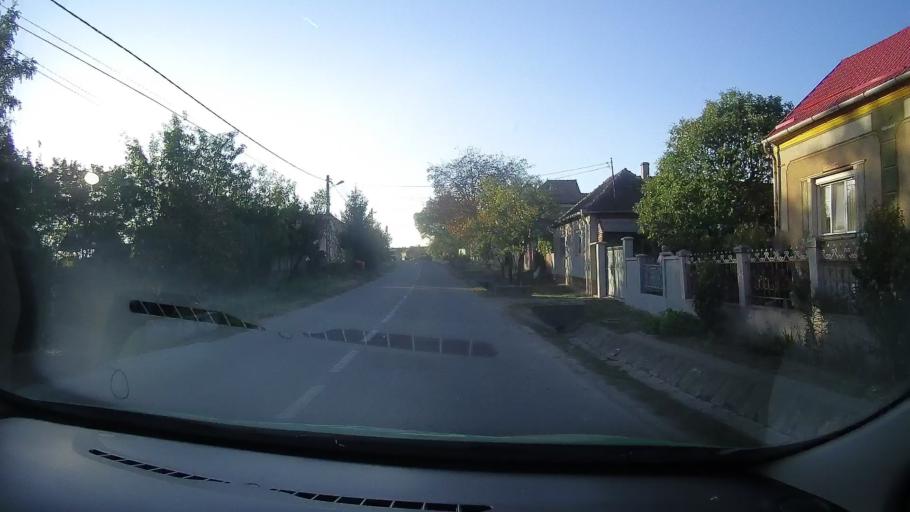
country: RO
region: Bihor
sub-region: Comuna Cetariu
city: Cetariu
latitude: 47.1474
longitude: 21.9984
